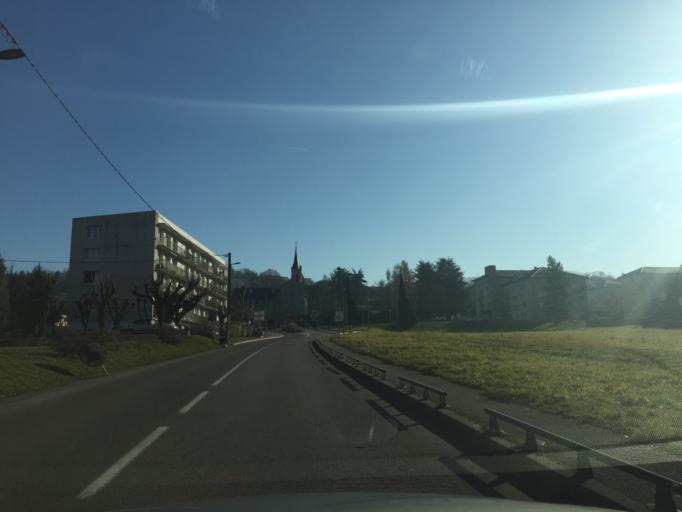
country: FR
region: Rhone-Alpes
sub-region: Departement de la Savoie
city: Jacob-Bellecombette
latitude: 45.5585
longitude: 5.9084
